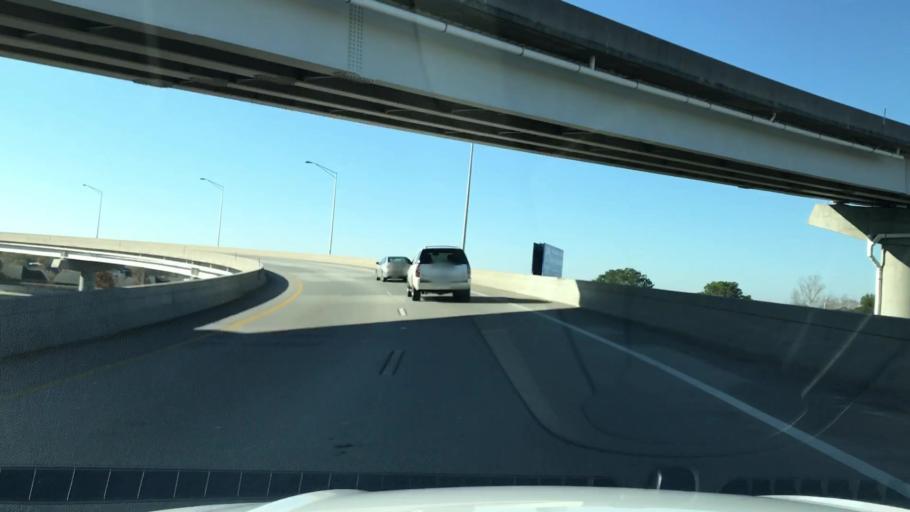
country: US
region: South Carolina
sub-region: Charleston County
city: Charleston
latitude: 32.8033
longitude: -79.9461
